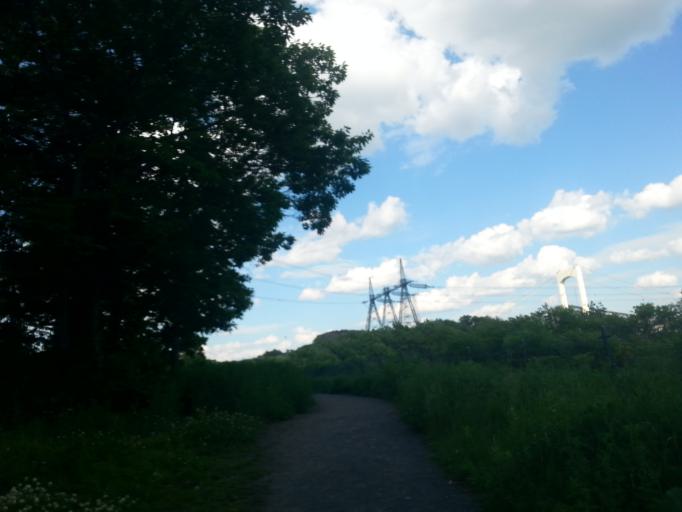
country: CA
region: Quebec
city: L'Ancienne-Lorette
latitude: 46.7495
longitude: -71.3004
